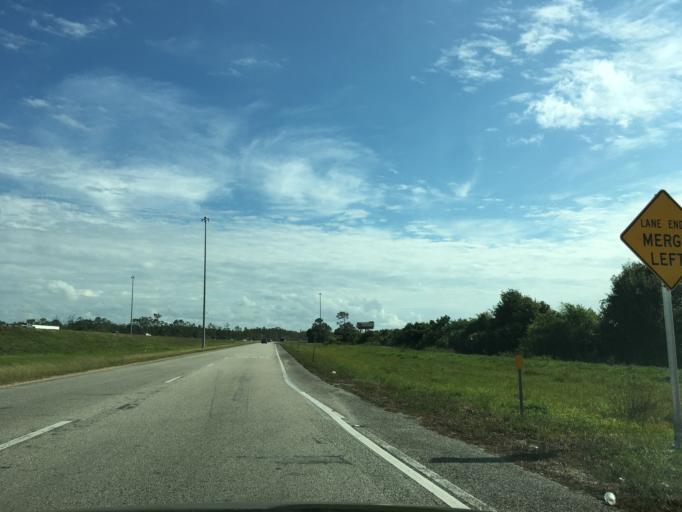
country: US
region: Florida
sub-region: Lee County
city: Fort Myers
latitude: 26.6120
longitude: -81.8042
